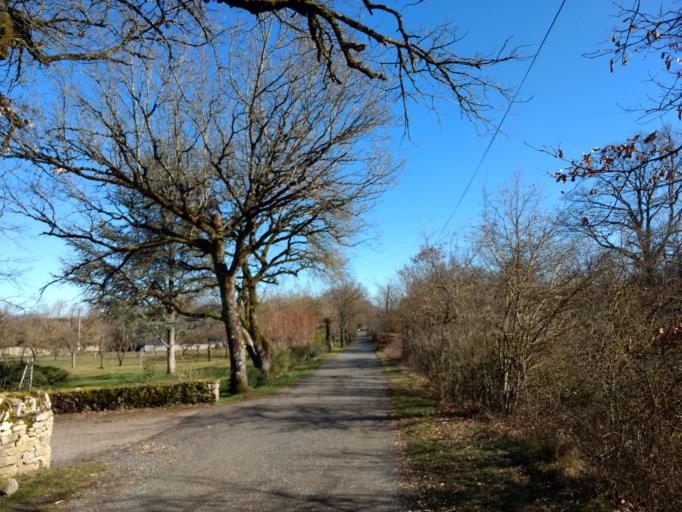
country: FR
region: Midi-Pyrenees
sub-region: Departement de l'Aveyron
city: Sebazac-Concoures
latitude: 44.4174
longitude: 2.5685
